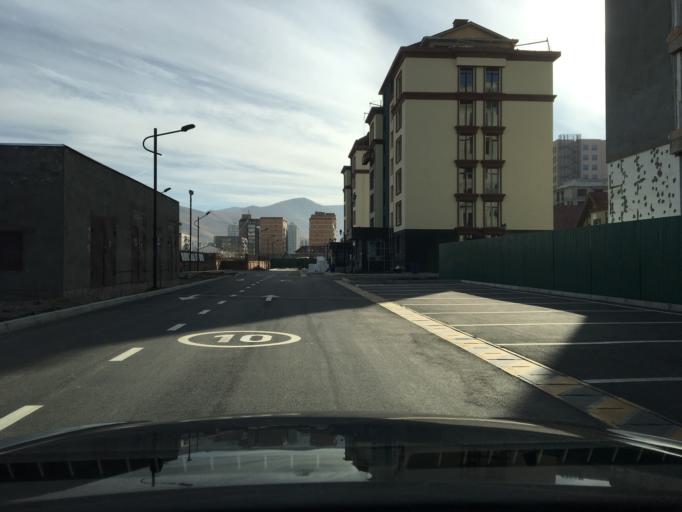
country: MN
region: Ulaanbaatar
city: Ulaanbaatar
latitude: 47.8985
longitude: 106.9121
